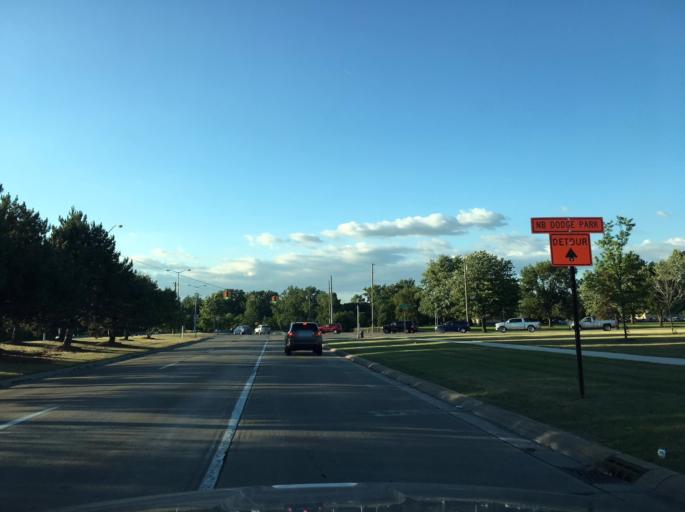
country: US
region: Michigan
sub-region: Macomb County
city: Sterling Heights
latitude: 42.5763
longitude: -82.9893
